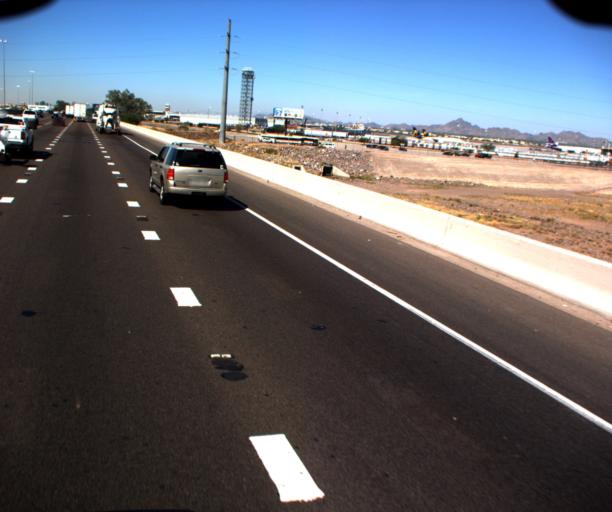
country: US
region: Arizona
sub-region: Maricopa County
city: Phoenix
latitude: 33.4188
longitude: -112.0178
